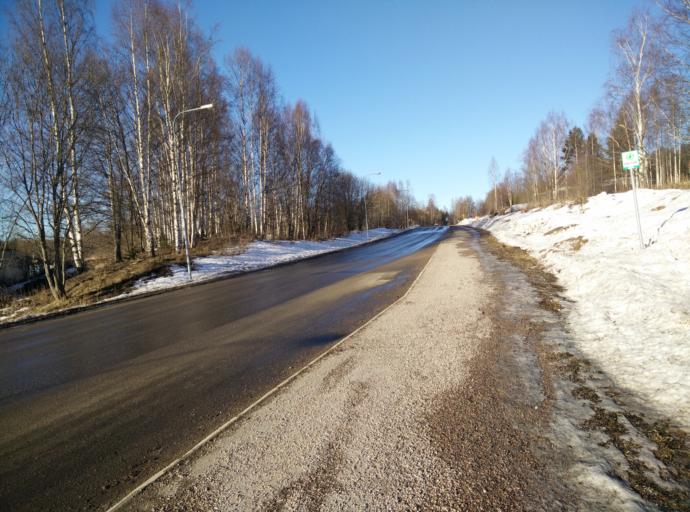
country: SE
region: Vaesternorrland
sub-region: Sundsvalls Kommun
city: Skottsund
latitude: 62.3128
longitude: 17.3929
